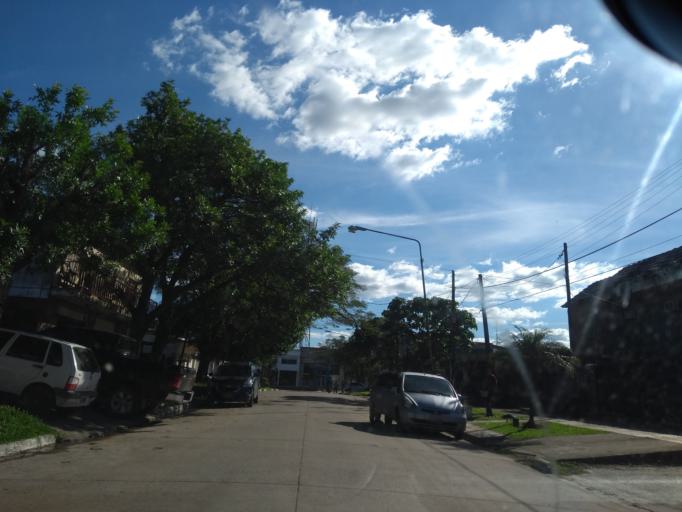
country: AR
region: Chaco
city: Barranqueras
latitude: -27.4744
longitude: -58.9589
